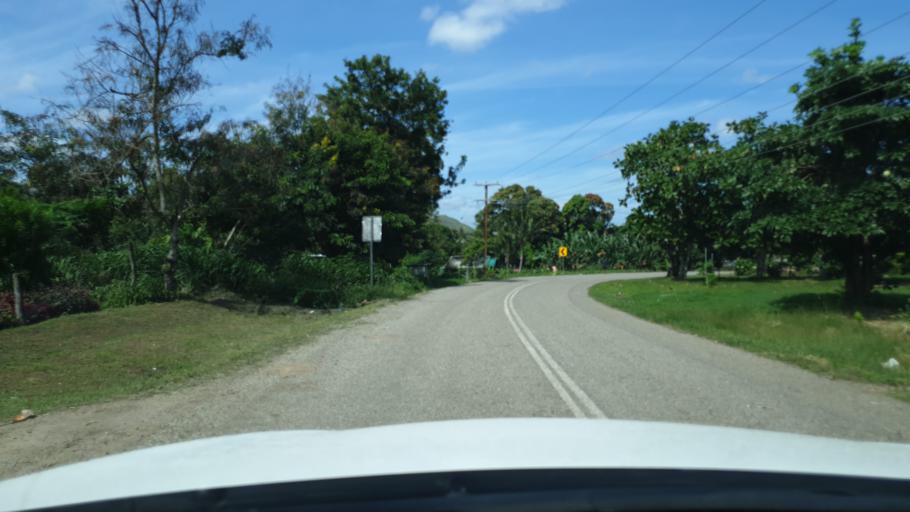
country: PG
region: Central Province
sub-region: Rigo
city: Kwikila
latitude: -9.8900
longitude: 147.5795
